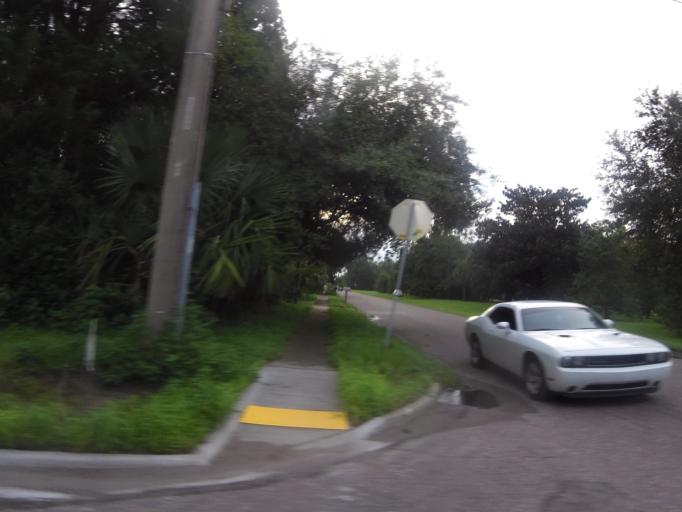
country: US
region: Florida
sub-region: Duval County
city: Jacksonville
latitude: 30.3511
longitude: -81.7164
